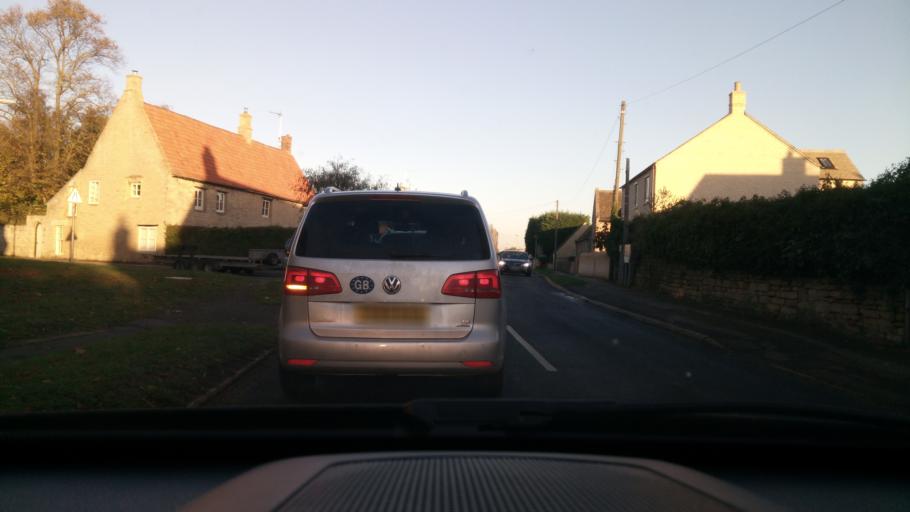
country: GB
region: England
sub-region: Peterborough
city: Helpston
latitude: 52.6354
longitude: -0.3433
